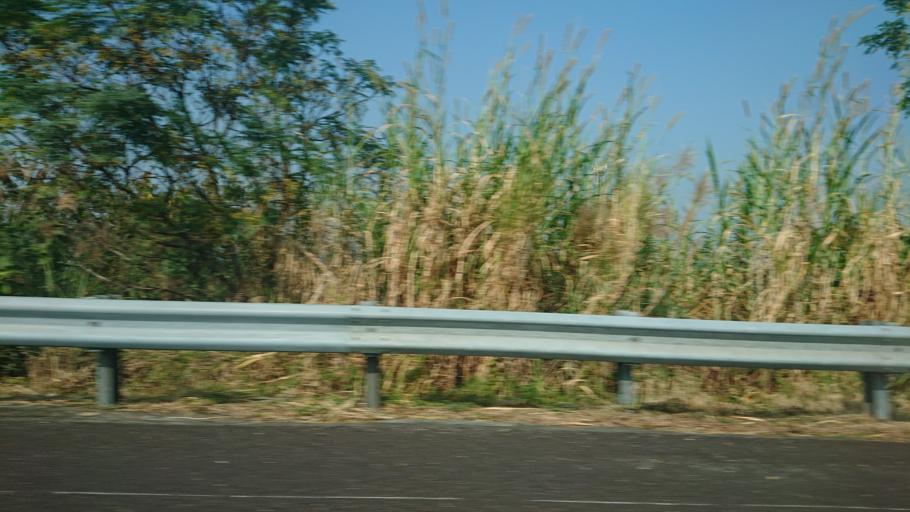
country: TW
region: Taiwan
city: Lugu
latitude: 23.8194
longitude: 120.7044
